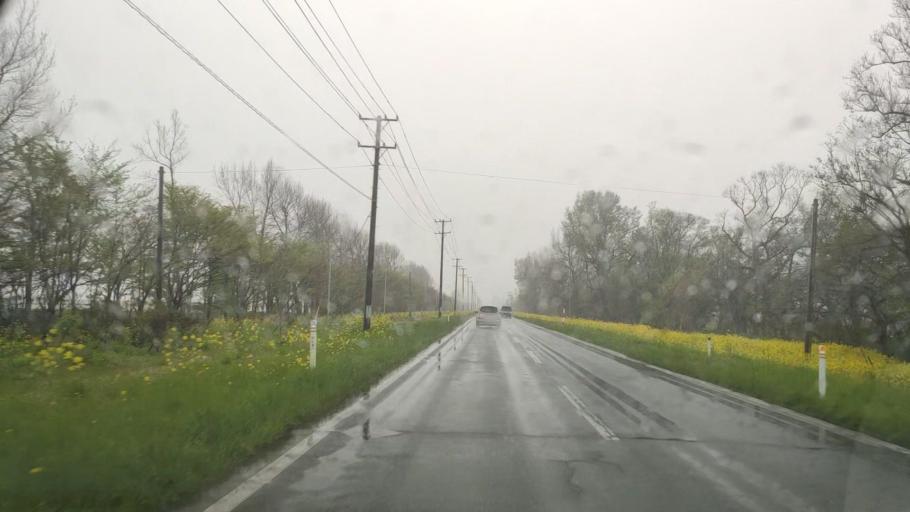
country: JP
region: Akita
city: Tenno
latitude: 39.9870
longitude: 139.9463
